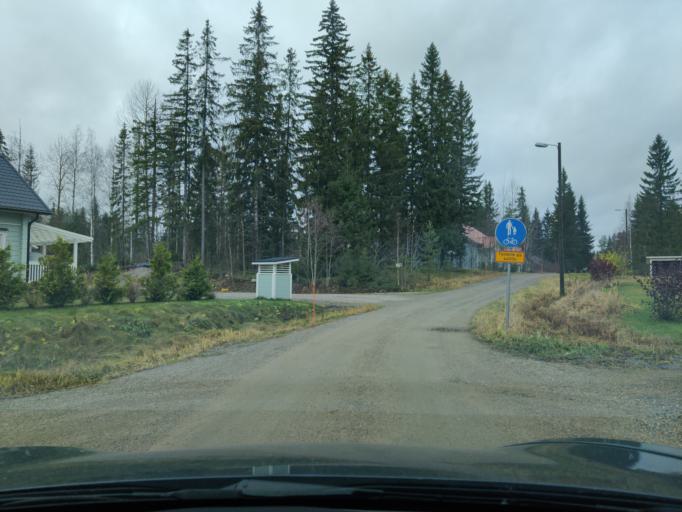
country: FI
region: Northern Savo
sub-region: Ylae-Savo
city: Kiuruvesi
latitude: 63.6397
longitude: 26.6399
